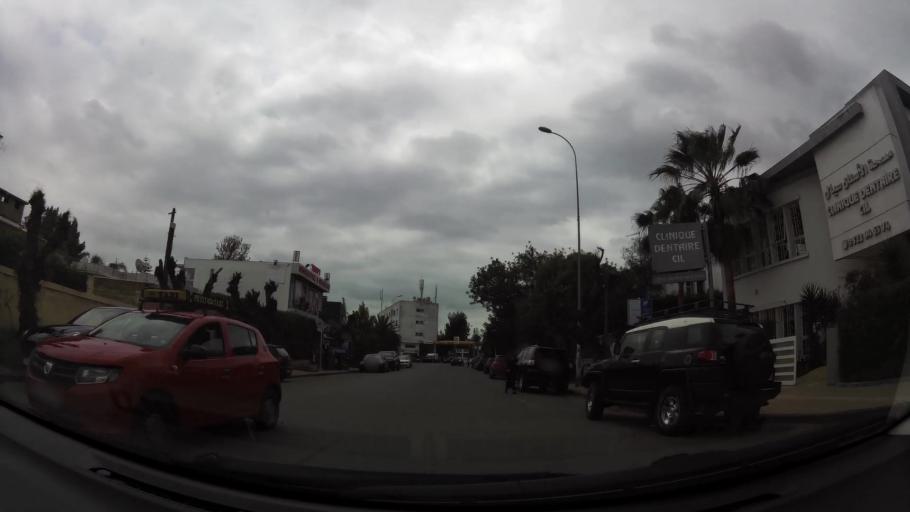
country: MA
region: Grand Casablanca
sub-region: Casablanca
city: Casablanca
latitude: 33.5743
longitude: -7.6559
